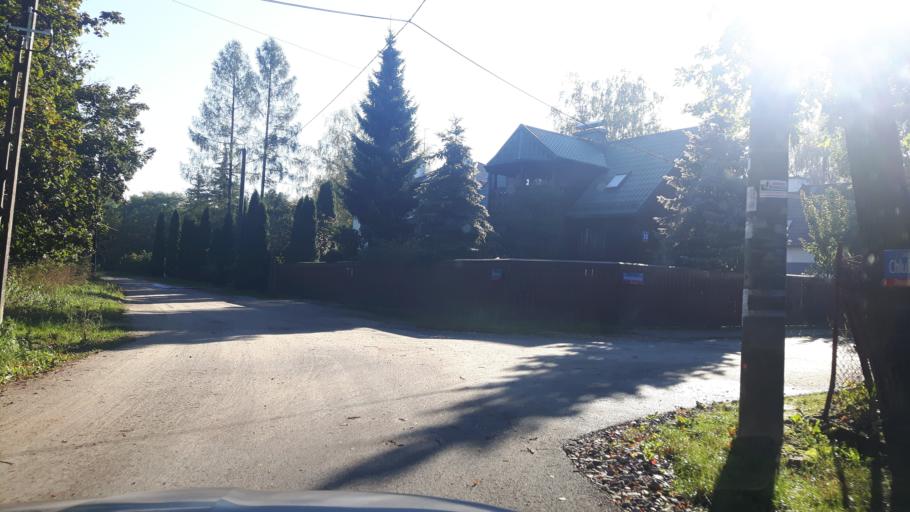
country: PL
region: Masovian Voivodeship
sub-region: Warszawa
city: Bialoleka
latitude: 52.3589
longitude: 20.9778
